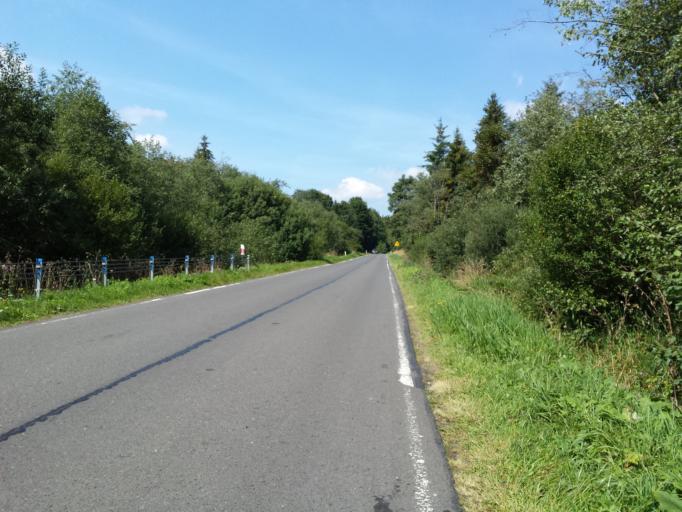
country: PL
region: Subcarpathian Voivodeship
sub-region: Powiat bieszczadzki
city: Lutowiska
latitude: 49.1093
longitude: 22.6247
